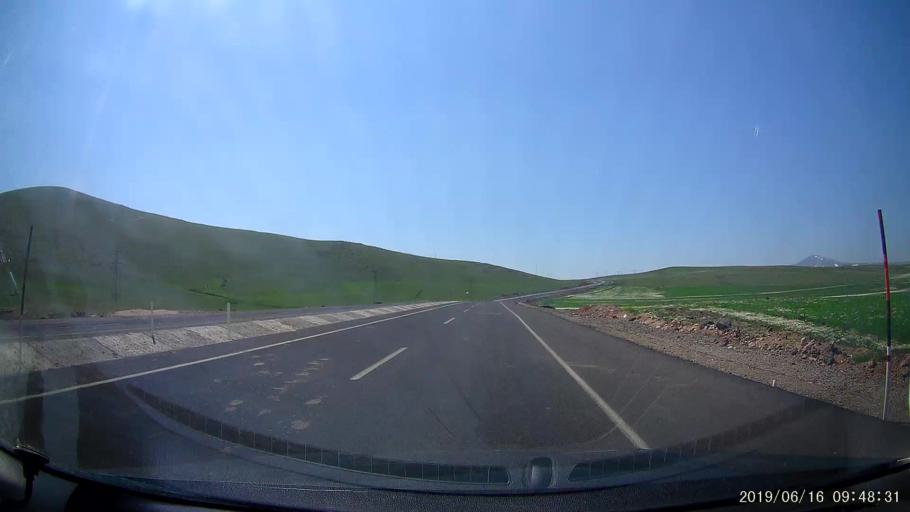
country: TR
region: Kars
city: Digor
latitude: 40.4328
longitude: 43.3537
